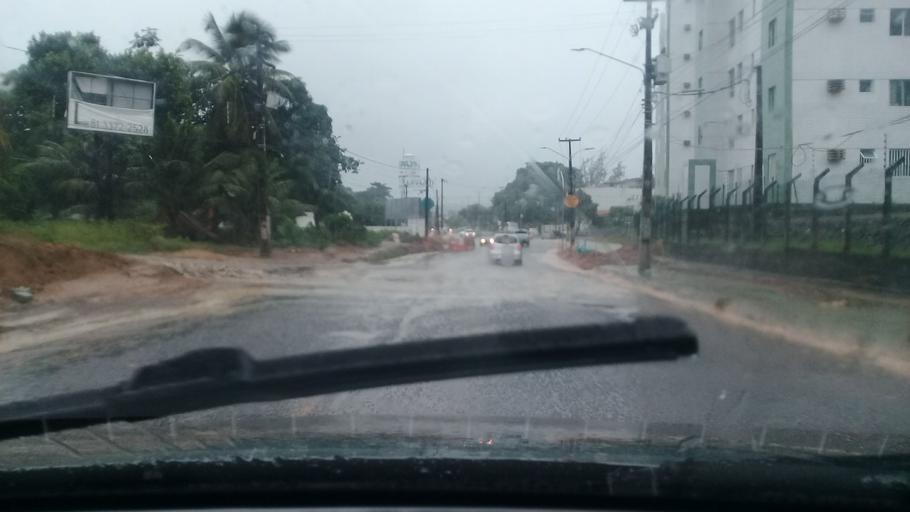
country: BR
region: Pernambuco
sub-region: Paulista
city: Paulista
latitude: -7.9483
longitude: -34.8886
